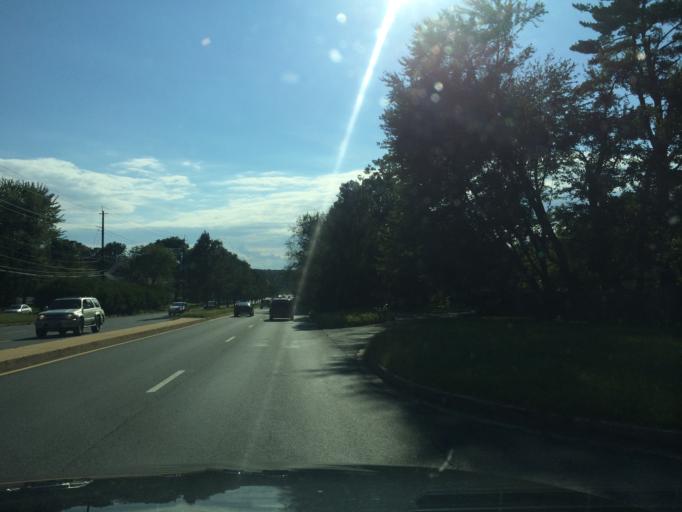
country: US
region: Maryland
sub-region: Montgomery County
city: Rossmoor
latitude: 39.0980
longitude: -77.1049
